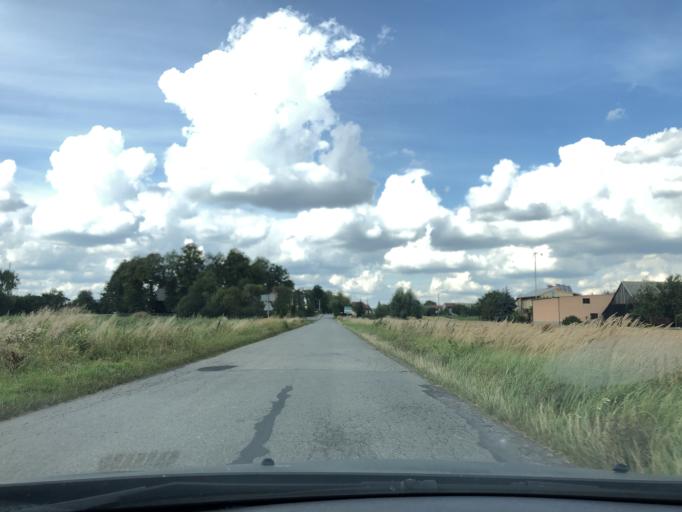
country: PL
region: Lodz Voivodeship
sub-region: Powiat wieruszowski
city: Walichnowy
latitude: 51.2581
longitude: 18.3942
